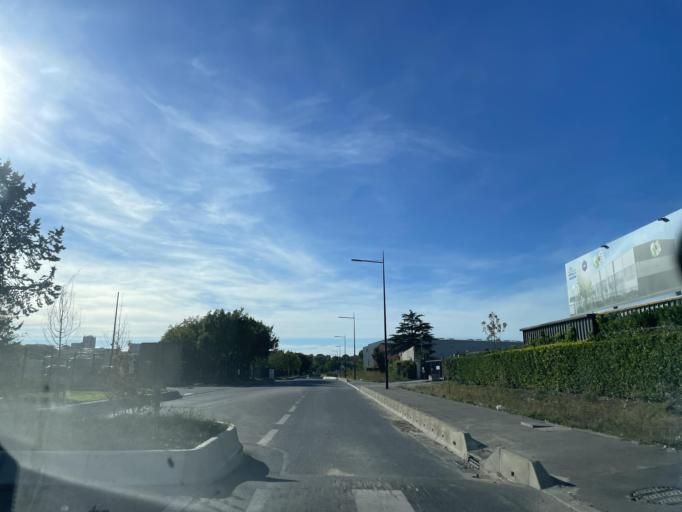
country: FR
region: Ile-de-France
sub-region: Departement du Val-de-Marne
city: Bonneuil-sur-Marne
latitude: 48.7799
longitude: 2.4876
